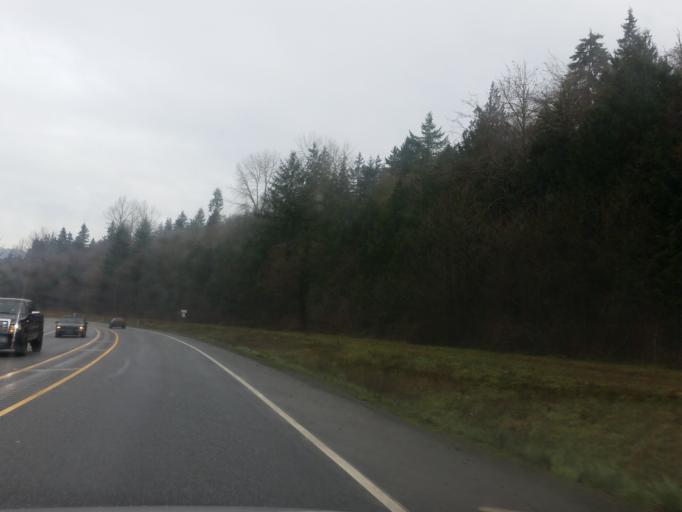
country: US
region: Washington
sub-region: Snohomish County
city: Cathcart
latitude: 47.8181
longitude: -122.0651
